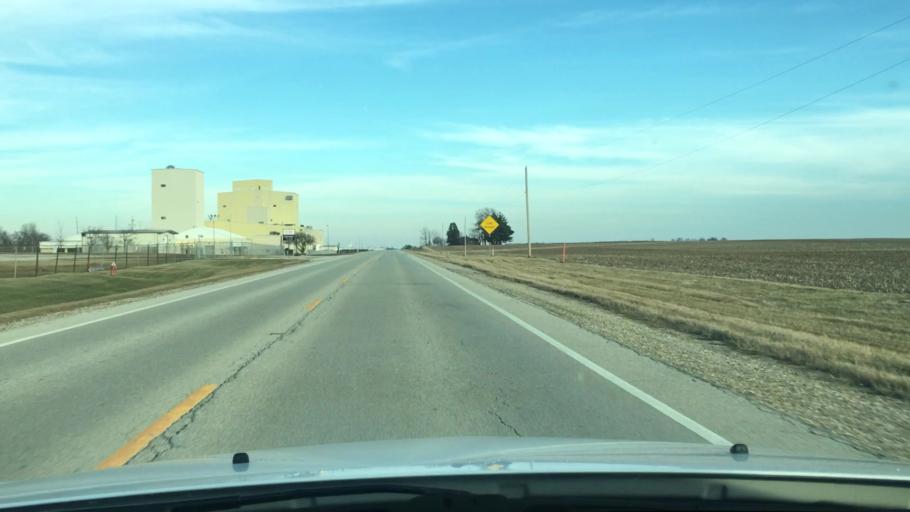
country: US
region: Illinois
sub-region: Woodford County
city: El Paso
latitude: 40.7376
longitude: -89.0020
